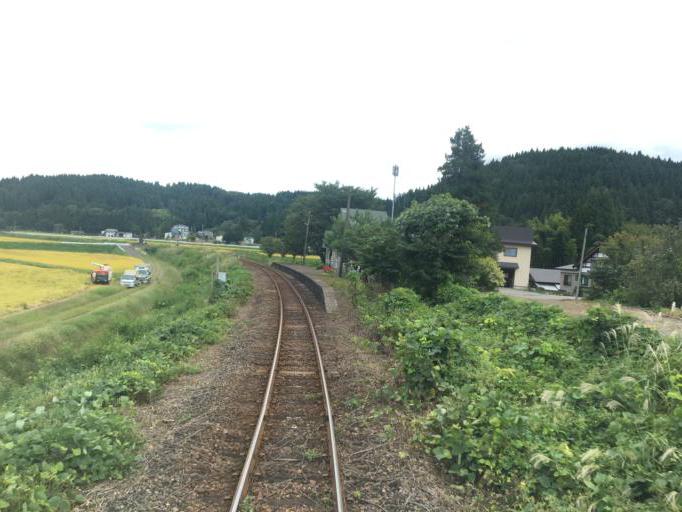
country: JP
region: Yamagata
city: Yuza
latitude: 39.2493
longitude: 140.1201
